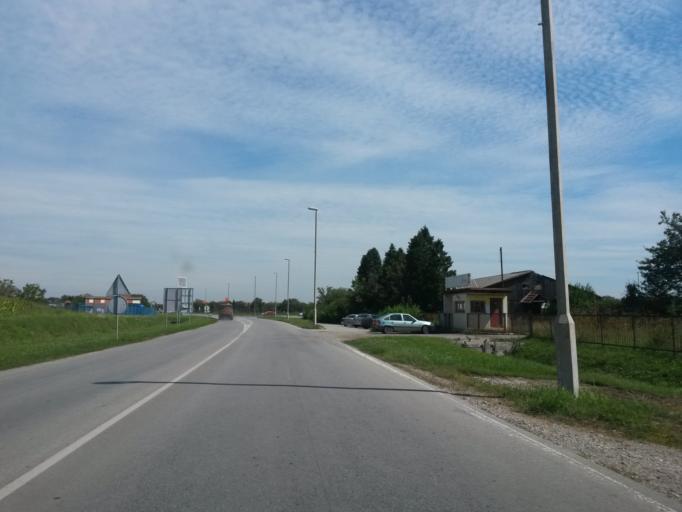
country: HR
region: Vukovarsko-Srijemska
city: Vinkovci
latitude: 45.2718
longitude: 18.7945
